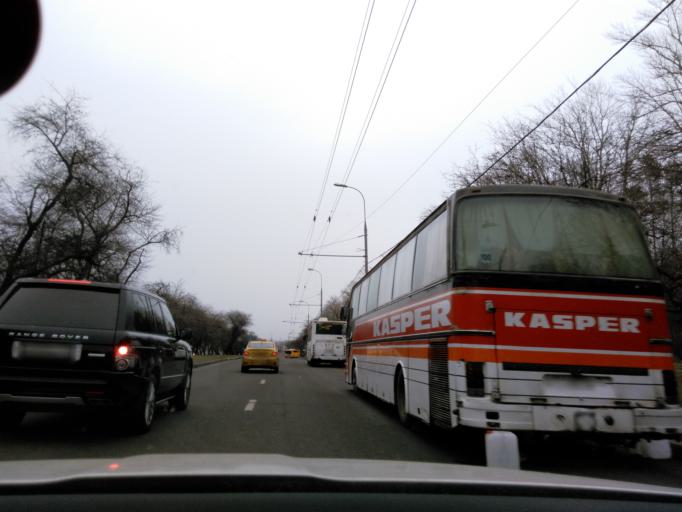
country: RU
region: Moscow
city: Vorob'yovo
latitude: 55.7127
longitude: 37.5295
